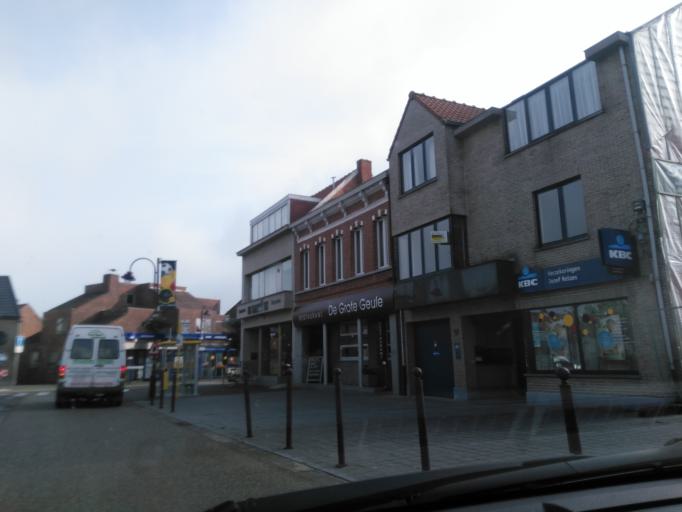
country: BE
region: Flanders
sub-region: Provincie Oost-Vlaanderen
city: Sint-Gillis-Waas
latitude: 51.2889
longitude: 4.1755
